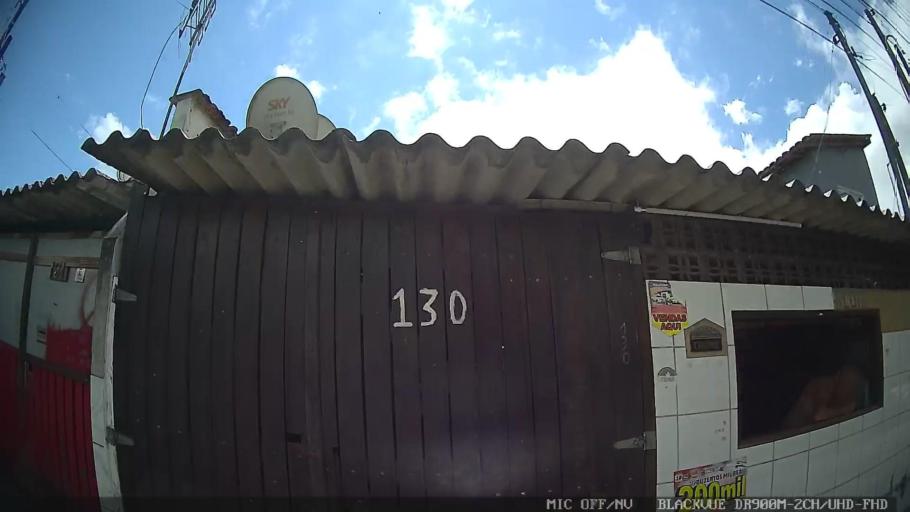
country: BR
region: Sao Paulo
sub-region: Caraguatatuba
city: Caraguatatuba
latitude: -23.6285
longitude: -45.4387
